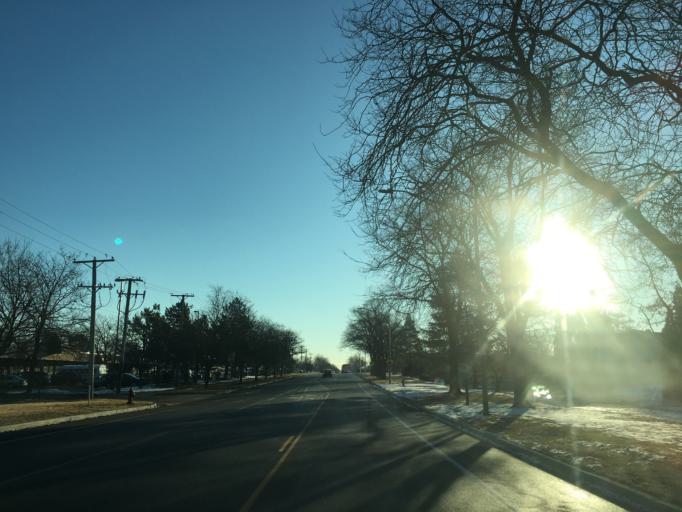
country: US
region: Illinois
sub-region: Cook County
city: Schaumburg
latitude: 42.0410
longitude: -88.1049
